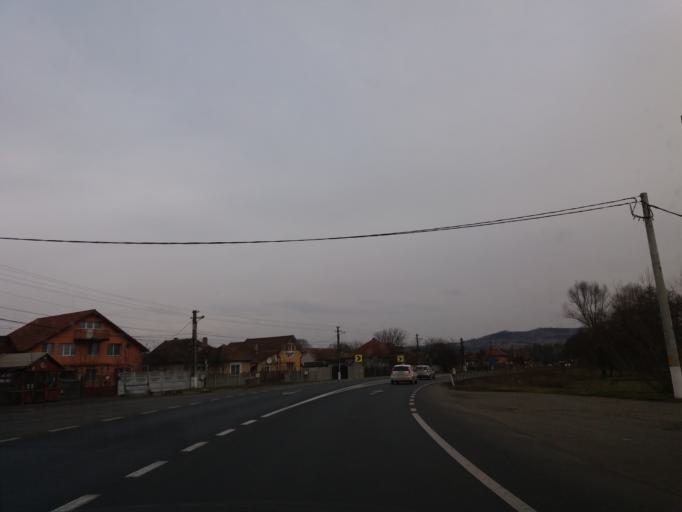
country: RO
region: Hunedoara
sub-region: Comuna Bacia
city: Bacia
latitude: 45.7991
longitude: 23.0045
